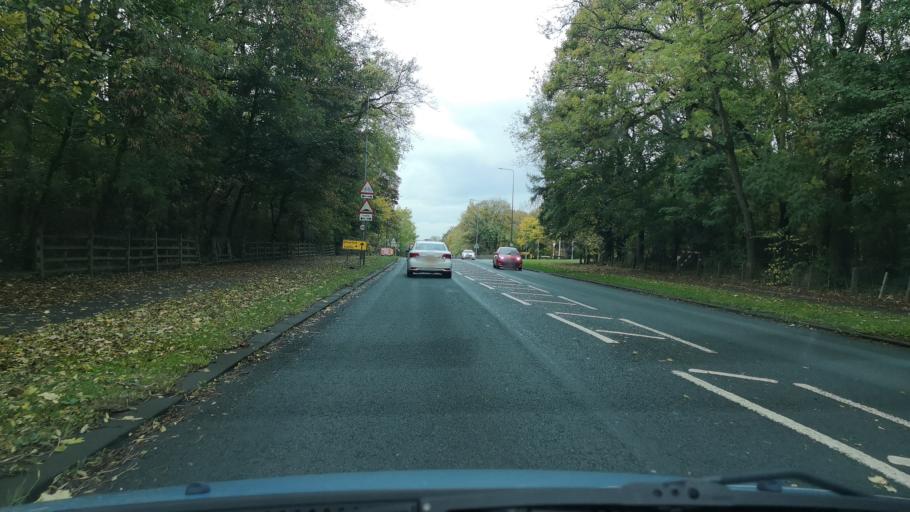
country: GB
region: England
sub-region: North Lincolnshire
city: Scunthorpe
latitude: 53.5833
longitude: -0.6714
